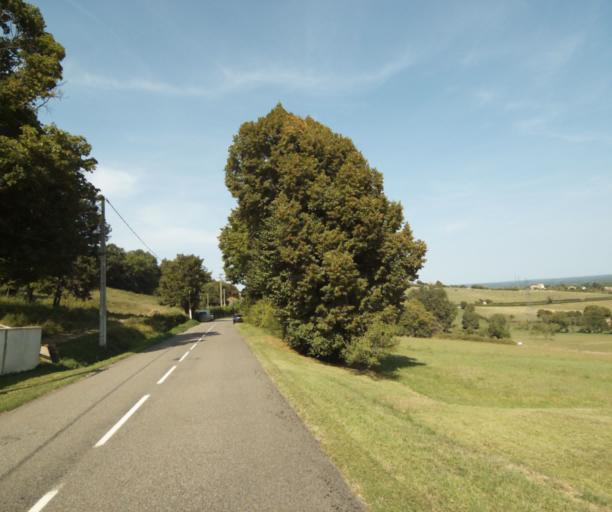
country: FR
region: Bourgogne
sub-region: Departement de Saone-et-Loire
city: Tournus
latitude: 46.5616
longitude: 4.8789
